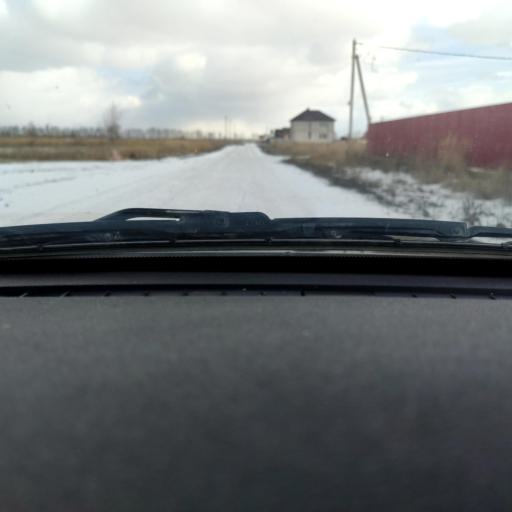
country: RU
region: Voronezj
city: Novaya Usman'
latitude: 51.6595
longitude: 39.4588
